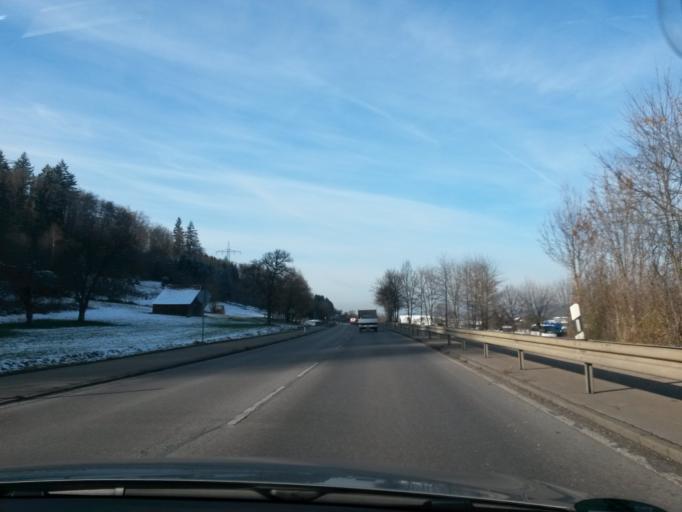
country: DE
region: Baden-Wuerttemberg
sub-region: Regierungsbezirk Stuttgart
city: Kuchen
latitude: 48.6459
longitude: 9.7885
